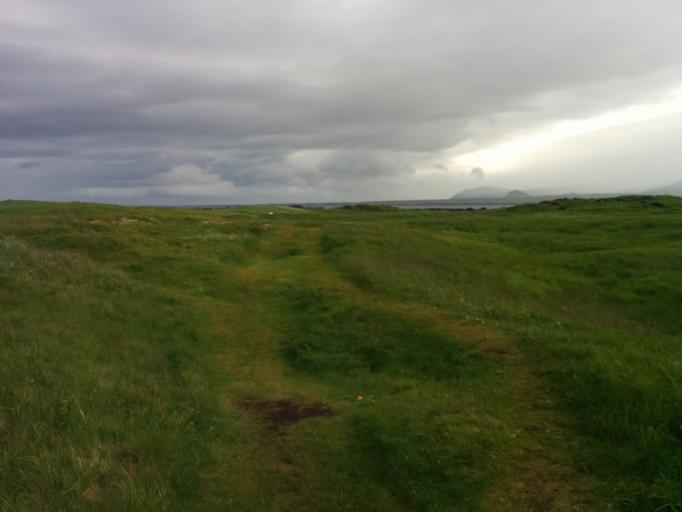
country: IS
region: West
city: Olafsvik
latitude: 64.8853
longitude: -24.0437
